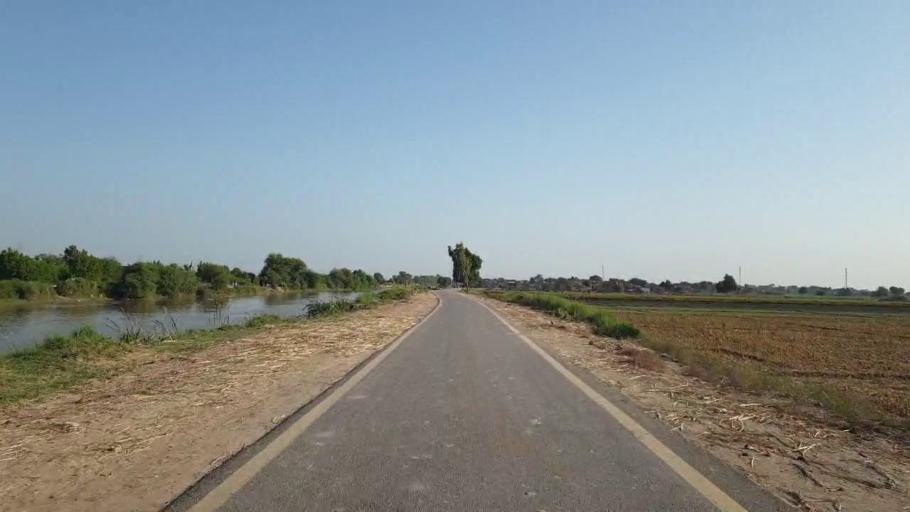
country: PK
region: Sindh
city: Hyderabad
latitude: 25.3273
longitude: 68.4251
